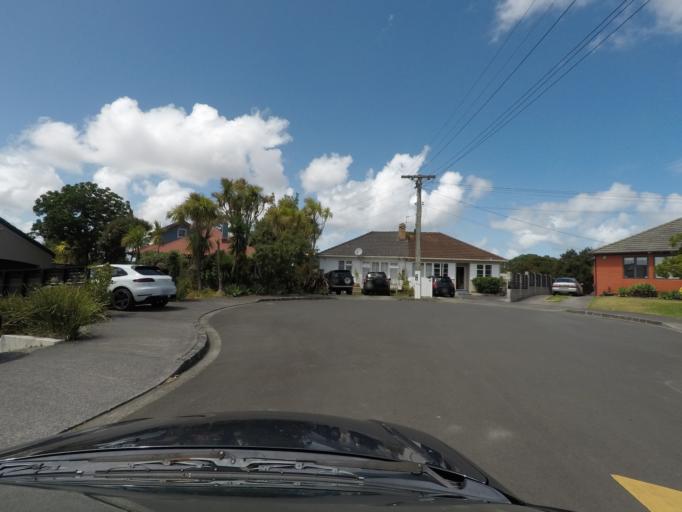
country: NZ
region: Auckland
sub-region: Auckland
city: Rosebank
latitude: -36.8573
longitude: 174.7077
